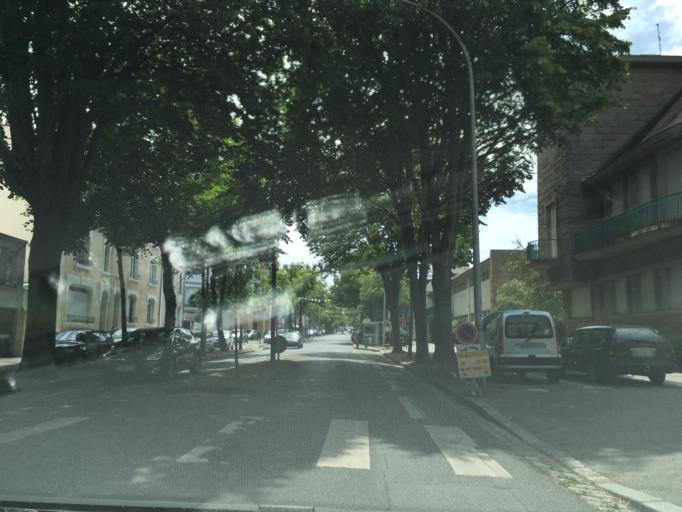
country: FR
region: Brittany
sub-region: Departement du Morbihan
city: Lorient
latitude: 47.7447
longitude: -3.3681
